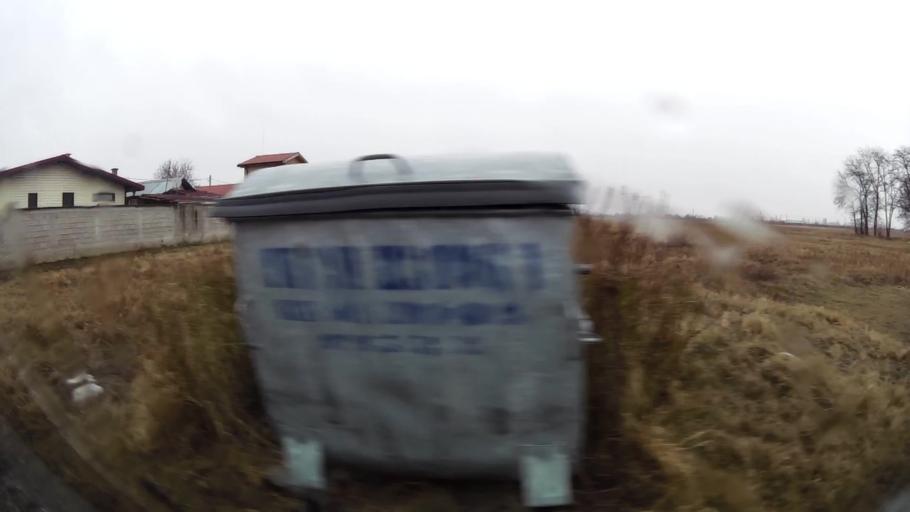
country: BG
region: Sofia-Capital
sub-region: Stolichna Obshtina
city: Sofia
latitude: 42.6577
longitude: 23.4291
